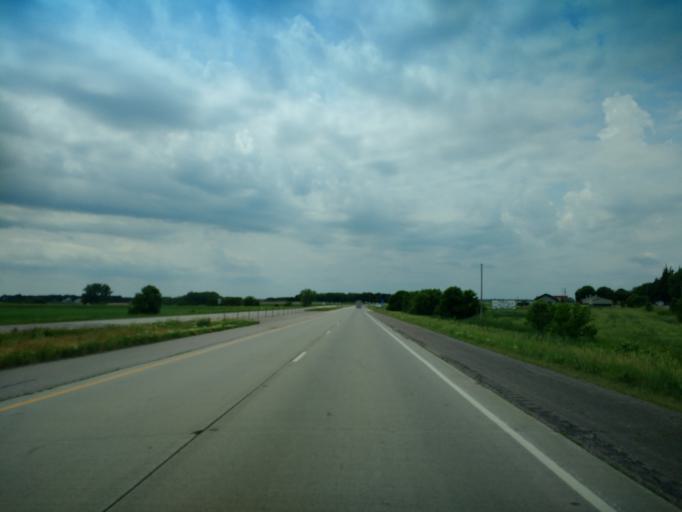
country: US
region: Minnesota
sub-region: Cottonwood County
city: Mountain Lake
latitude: 43.9535
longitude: -94.7902
